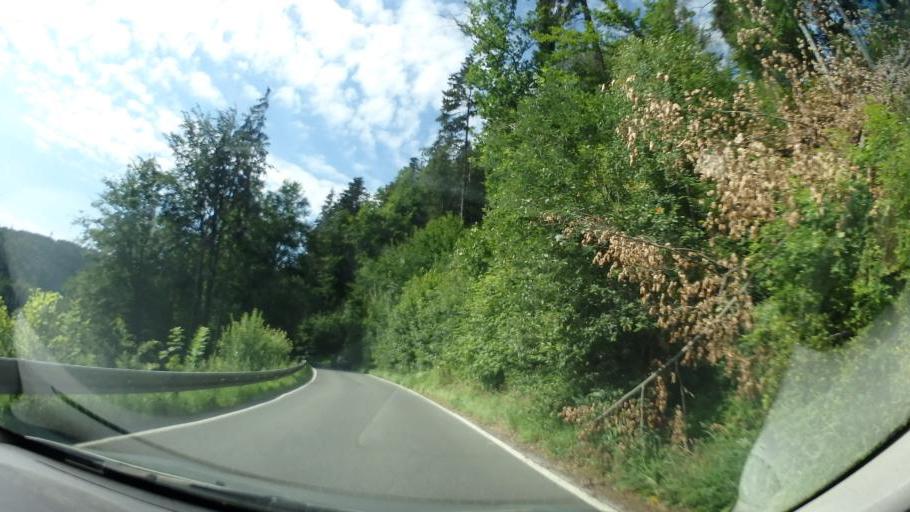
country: CZ
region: Olomoucky
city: Zabreh
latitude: 49.8655
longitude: 16.8287
